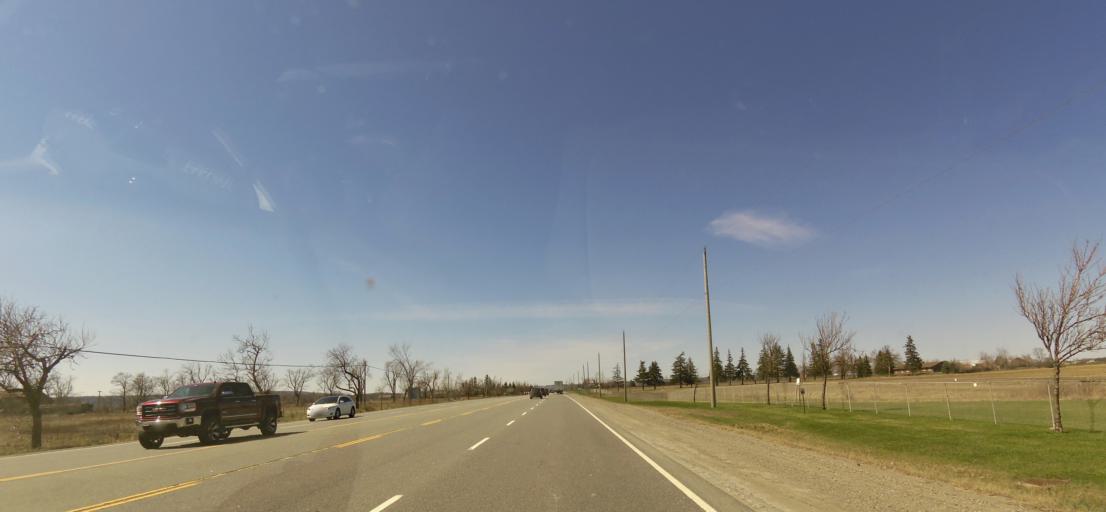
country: CA
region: Ontario
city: Brampton
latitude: 43.7777
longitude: -79.8839
